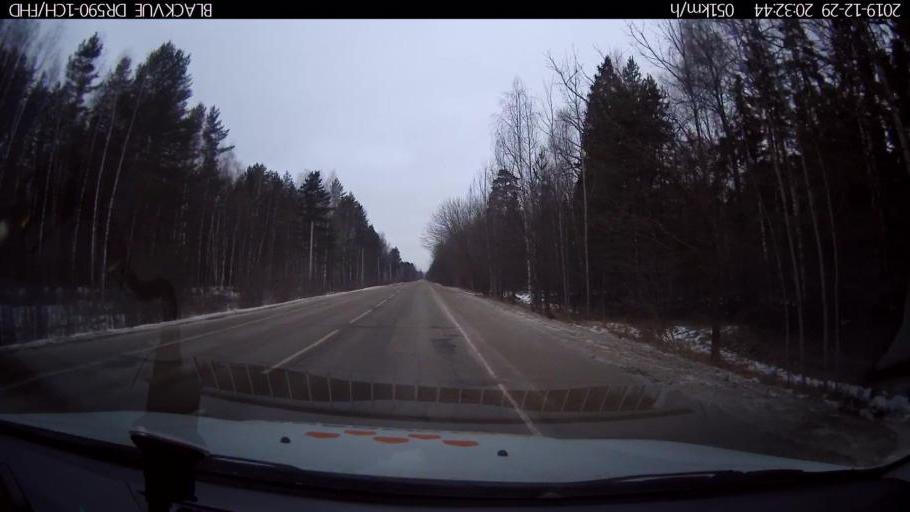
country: RU
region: Nizjnij Novgorod
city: Afonino
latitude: 56.1768
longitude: 44.0604
